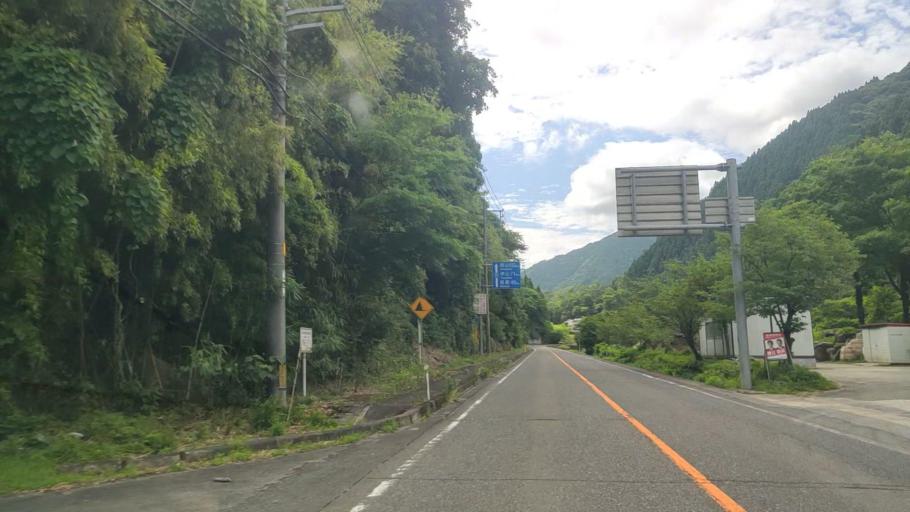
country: JP
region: Tottori
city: Yonago
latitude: 35.2265
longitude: 133.4458
